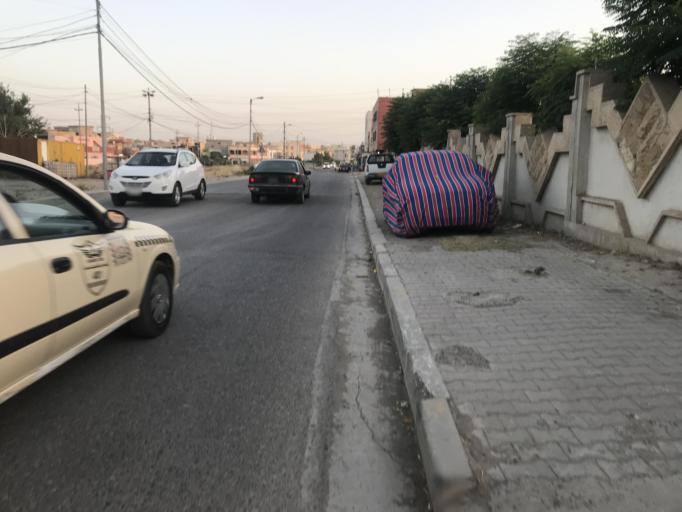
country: IQ
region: Dahuk
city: Saymayl
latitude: 36.8596
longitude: 42.8360
